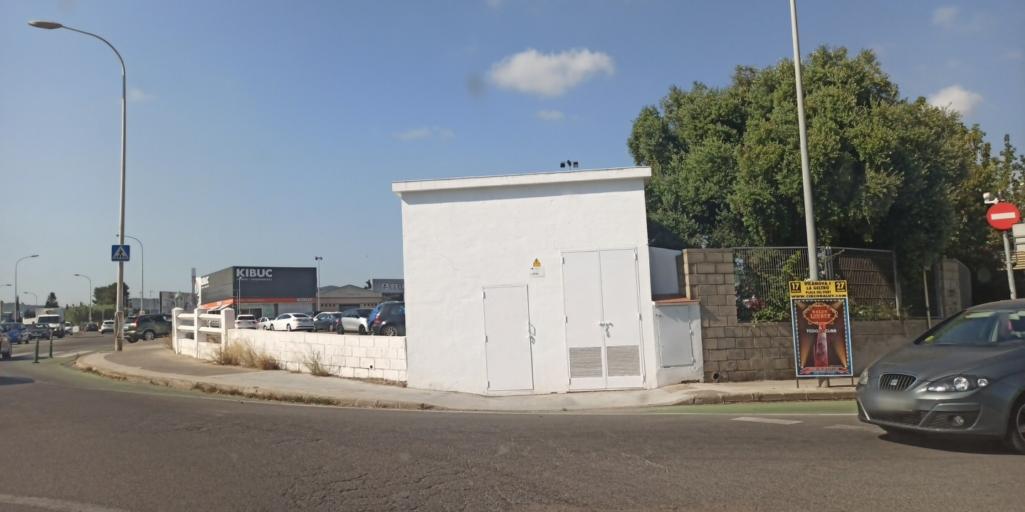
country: ES
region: Catalonia
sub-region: Provincia de Barcelona
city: Vilanova i la Geltru
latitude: 41.2262
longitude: 1.7401
